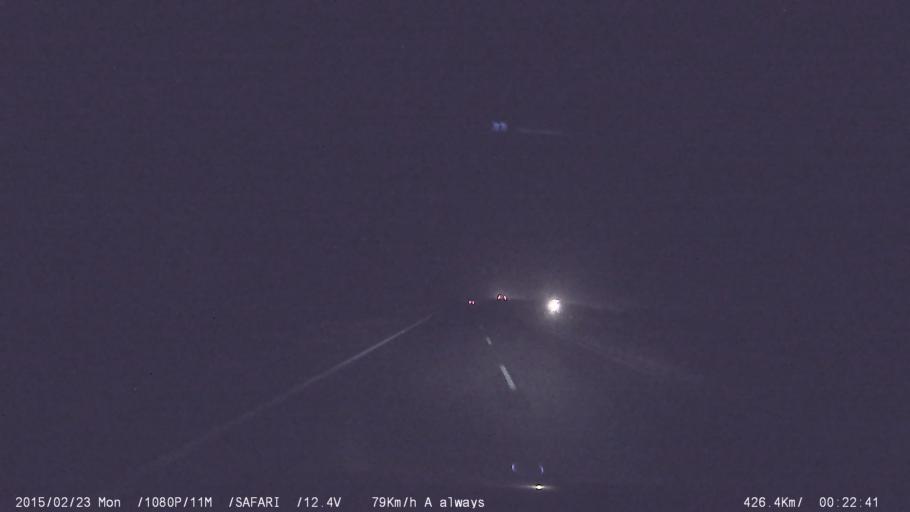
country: IN
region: Tamil Nadu
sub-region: Salem
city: Omalur
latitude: 11.9148
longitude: 78.0592
